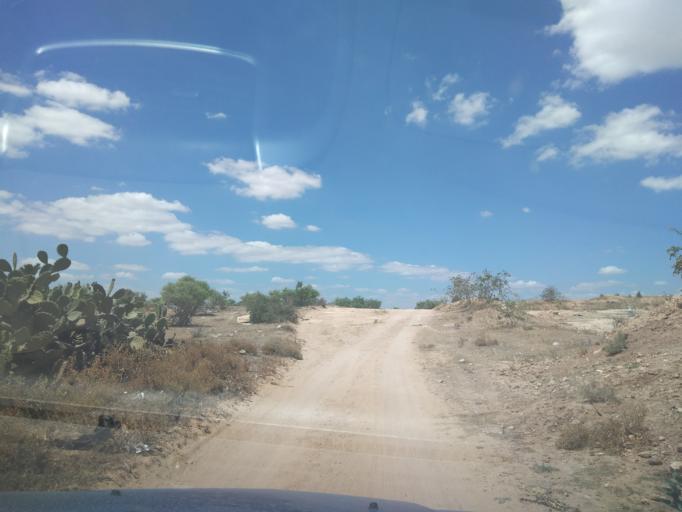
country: TN
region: Susah
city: Harqalah
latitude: 36.1653
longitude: 10.4464
